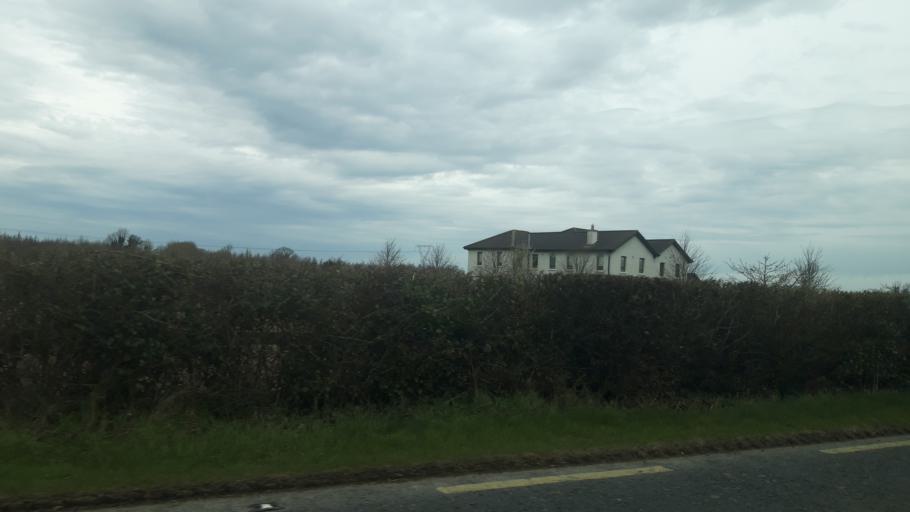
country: IE
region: Leinster
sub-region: Kildare
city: Clane
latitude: 53.3148
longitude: -6.6456
